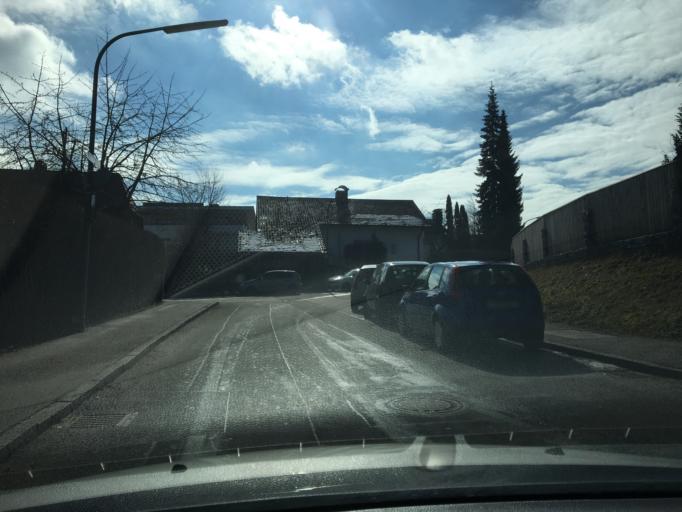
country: DE
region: Bavaria
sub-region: Lower Bavaria
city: Landshut
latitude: 48.5328
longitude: 12.1649
